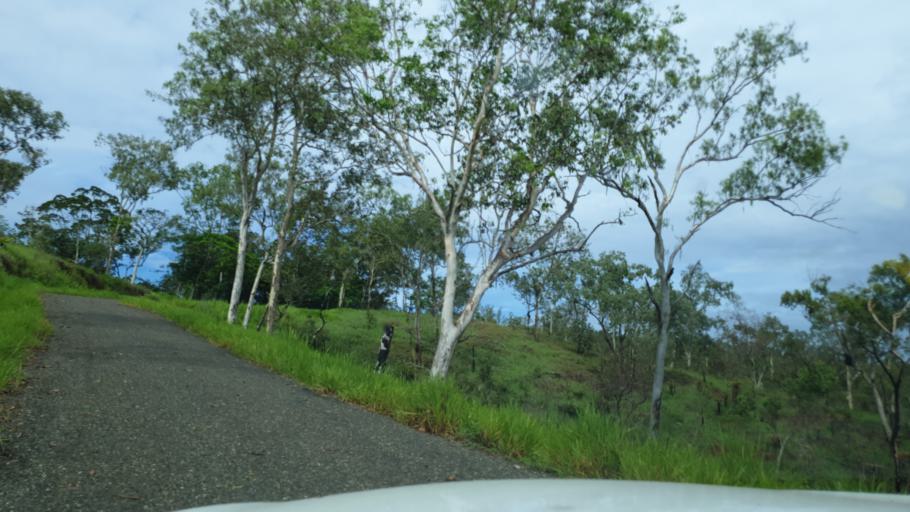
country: PG
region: National Capital
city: Port Moresby
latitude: -9.4350
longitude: 147.3843
